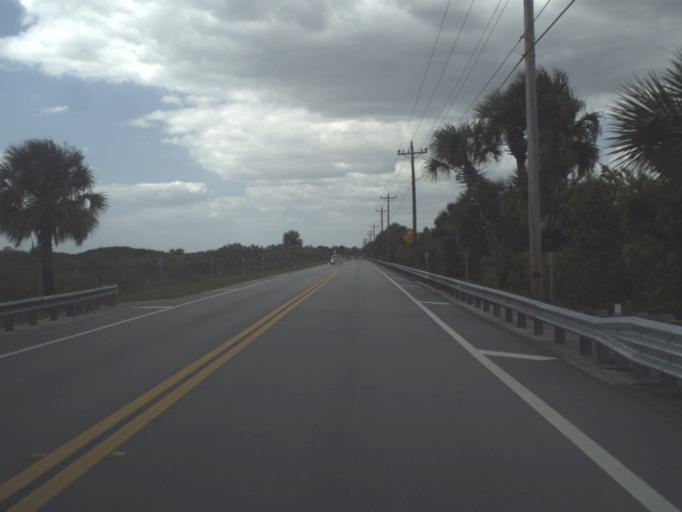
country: US
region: Florida
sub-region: Collier County
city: Marco
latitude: 25.9524
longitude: -81.4845
